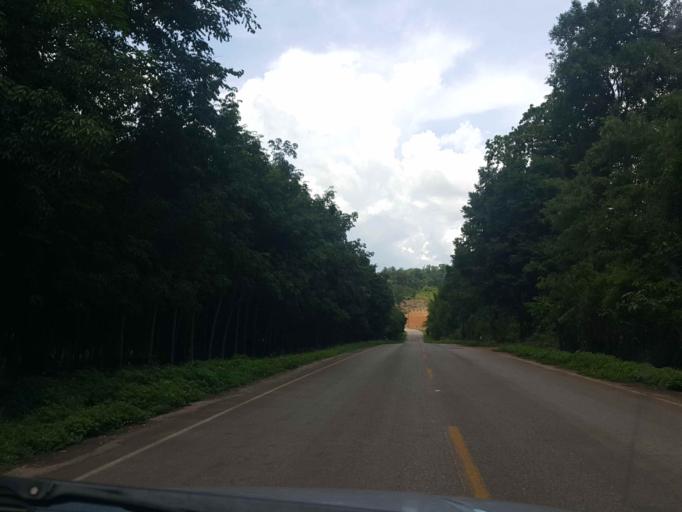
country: TH
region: Phayao
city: Chiang Muan
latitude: 18.9022
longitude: 100.1240
